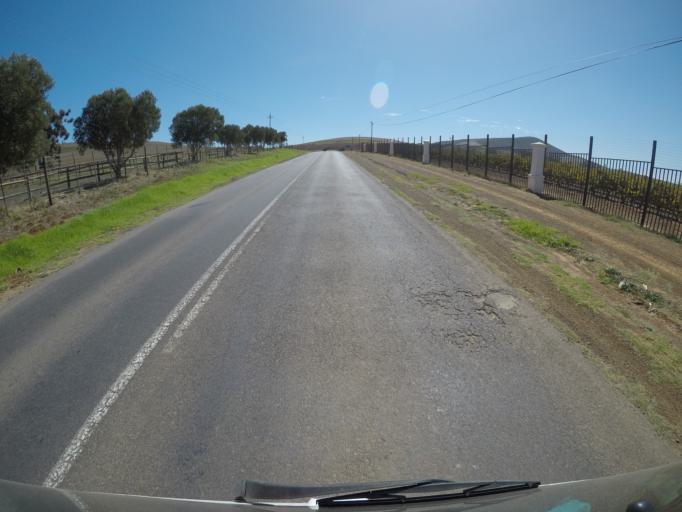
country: ZA
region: Western Cape
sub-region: City of Cape Town
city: Kraaifontein
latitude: -33.8062
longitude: 18.6224
